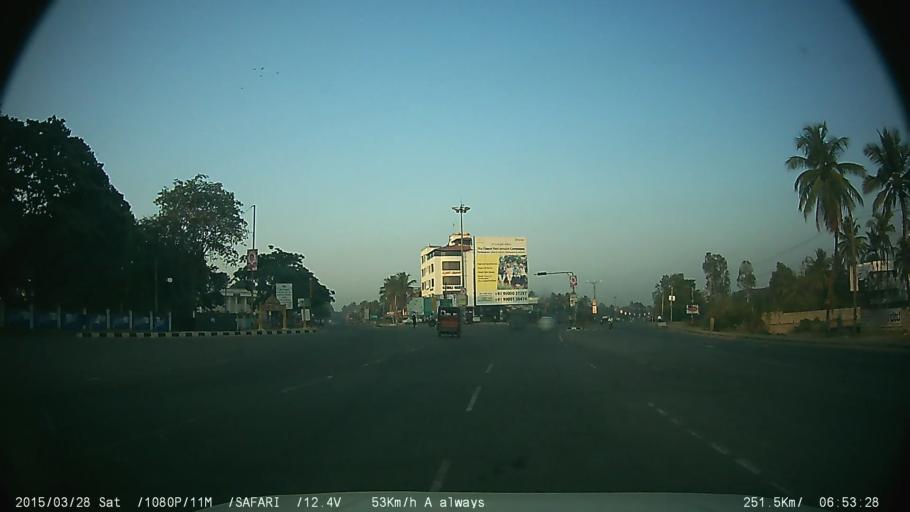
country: IN
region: Karnataka
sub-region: Mandya
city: Maddur
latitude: 12.5831
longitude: 77.0378
